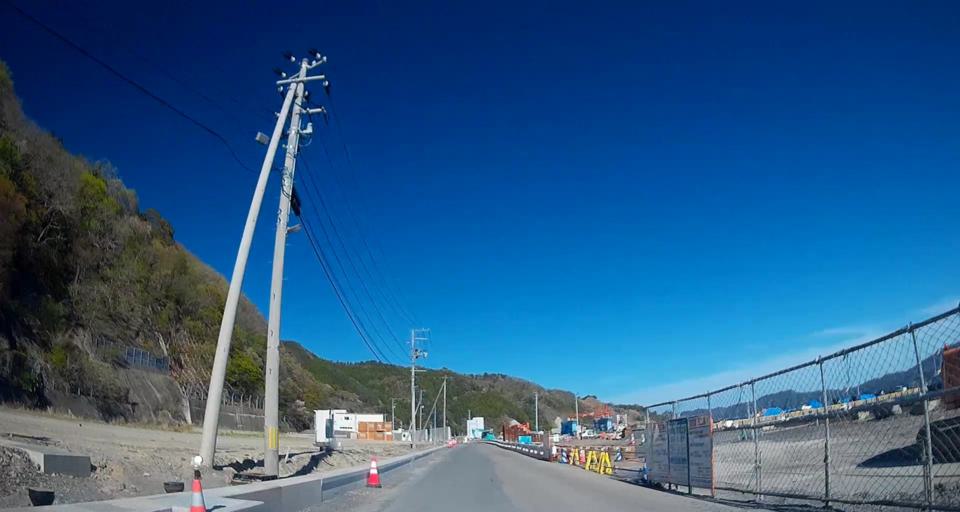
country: JP
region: Iwate
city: Kamaishi
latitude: 39.2718
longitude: 141.8960
